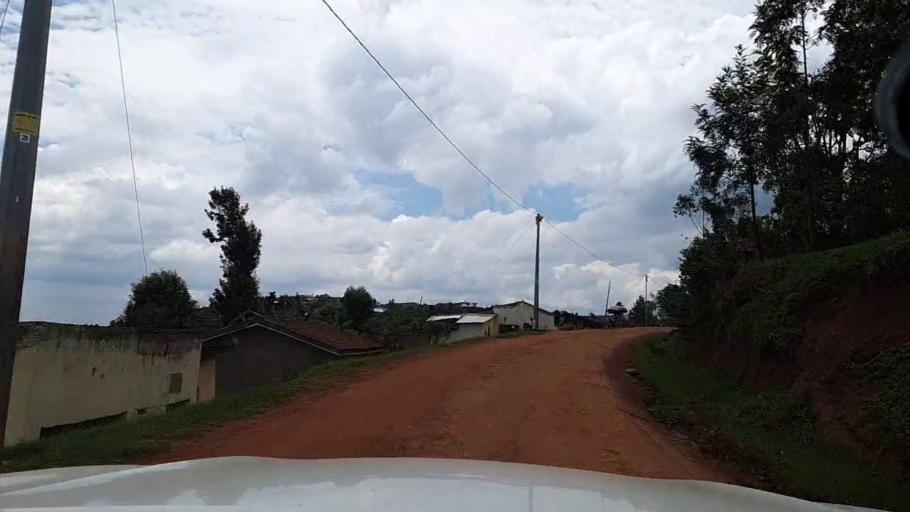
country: BI
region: Kayanza
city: Kayanza
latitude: -2.7117
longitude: 29.5413
